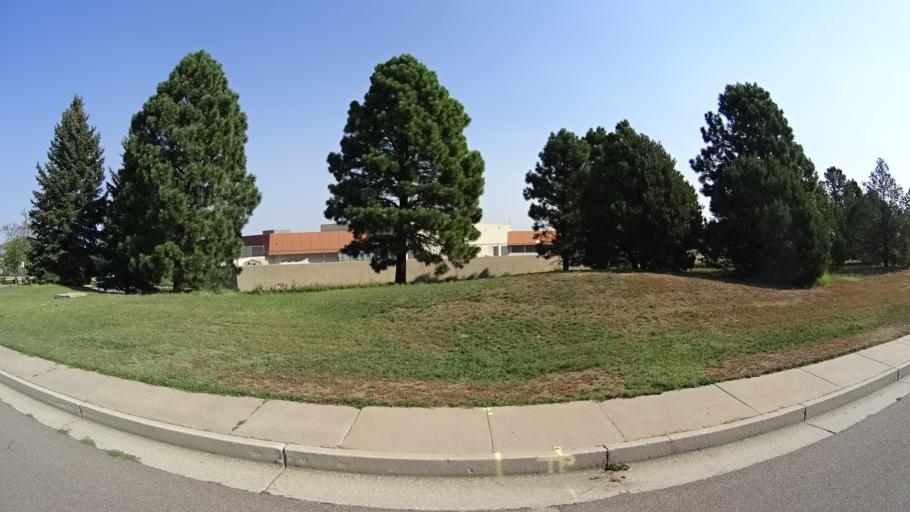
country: US
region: Colorado
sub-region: El Paso County
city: Stratmoor
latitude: 38.7813
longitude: -104.8048
